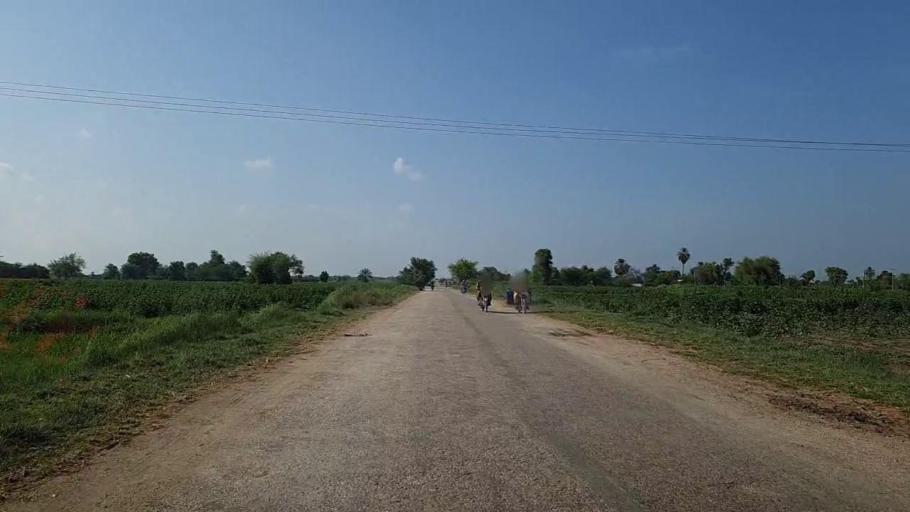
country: PK
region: Sindh
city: Kandiaro
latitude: 27.0575
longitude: 68.3170
